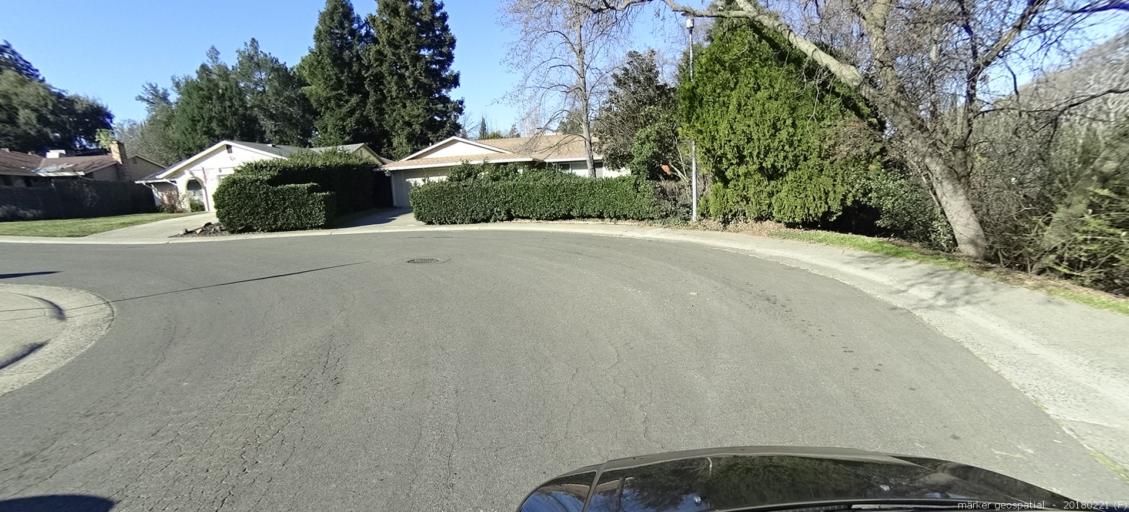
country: US
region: California
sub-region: Sacramento County
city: Orangevale
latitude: 38.6840
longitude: -121.2506
